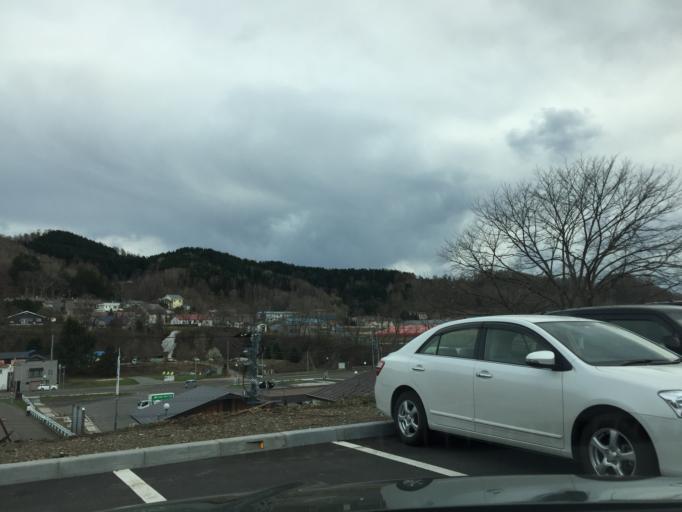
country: JP
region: Hokkaido
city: Utashinai
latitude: 43.5038
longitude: 142.0063
